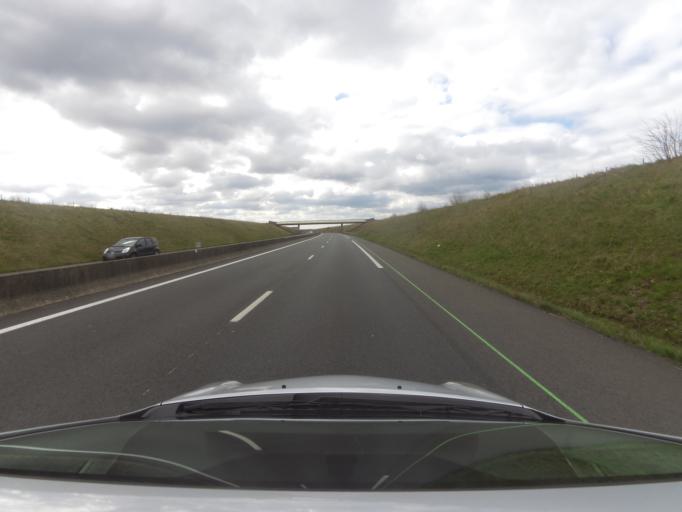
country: FR
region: Nord-Pas-de-Calais
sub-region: Departement du Pas-de-Calais
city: Verton
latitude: 50.3603
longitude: 1.6890
